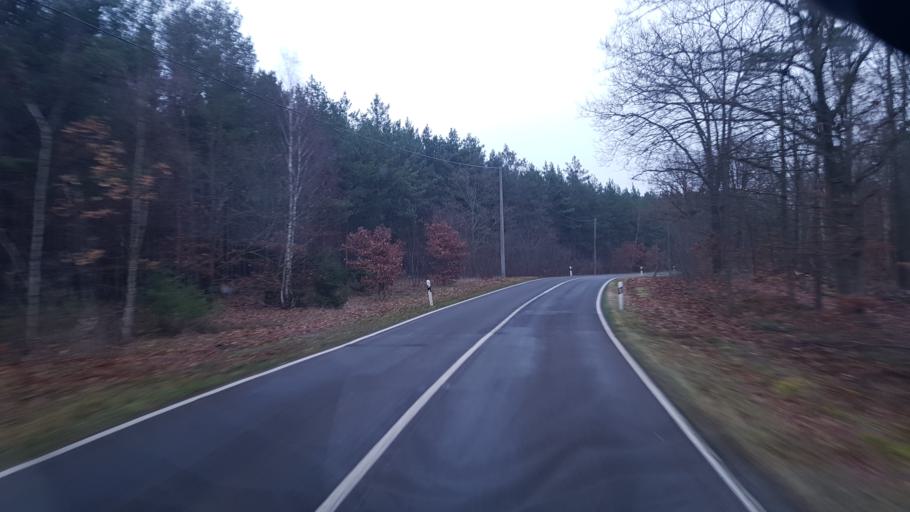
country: DE
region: Brandenburg
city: Drachhausen
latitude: 51.8869
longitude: 14.3021
